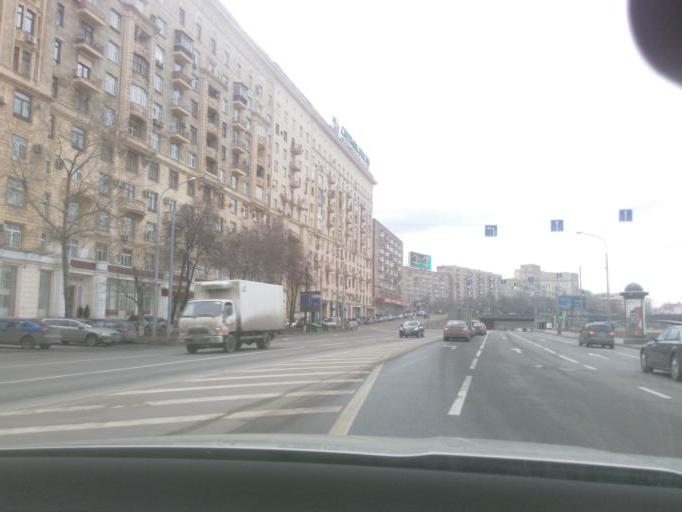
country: RU
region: Moskovskaya
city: Dorogomilovo
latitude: 55.7482
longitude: 37.5761
